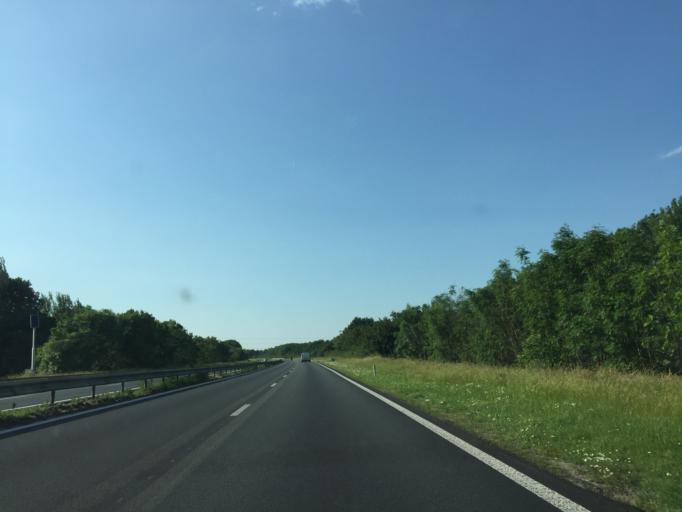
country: NL
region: Gelderland
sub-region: Gemeente Buren
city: Lienden
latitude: 51.9008
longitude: 5.4963
